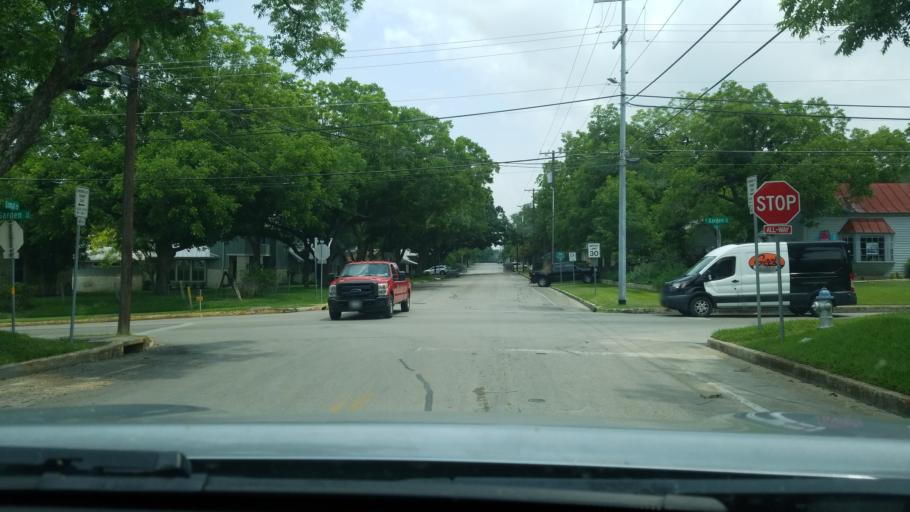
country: US
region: Texas
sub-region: Comal County
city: New Braunfels
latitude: 29.7014
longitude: -98.1200
